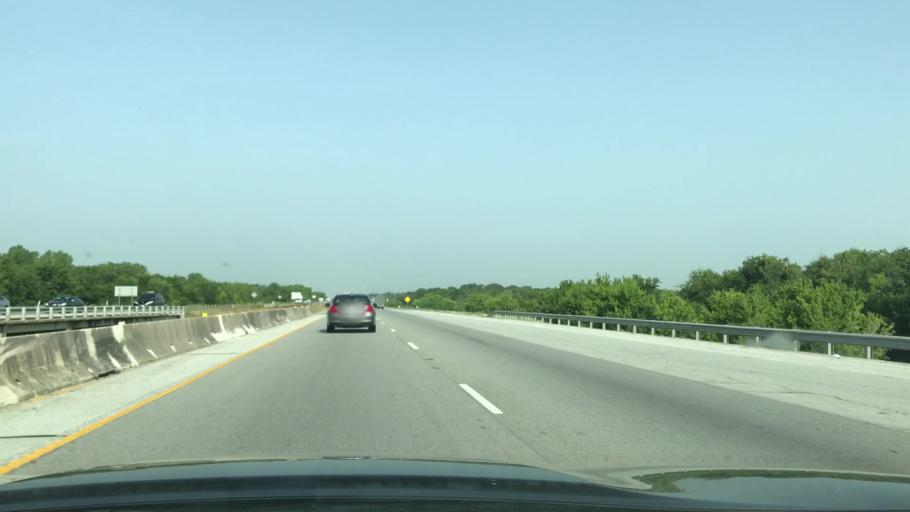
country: US
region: Texas
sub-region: Kaufman County
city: Forney
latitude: 32.7726
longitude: -96.4939
